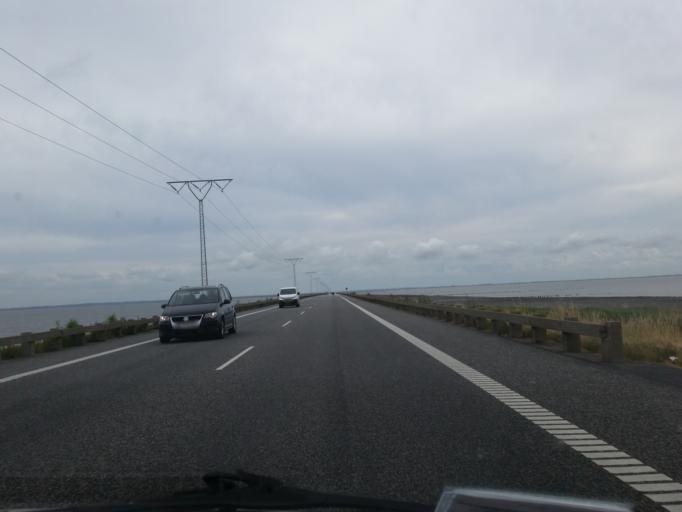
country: DE
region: Schleswig-Holstein
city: List
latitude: 55.1514
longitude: 8.5686
